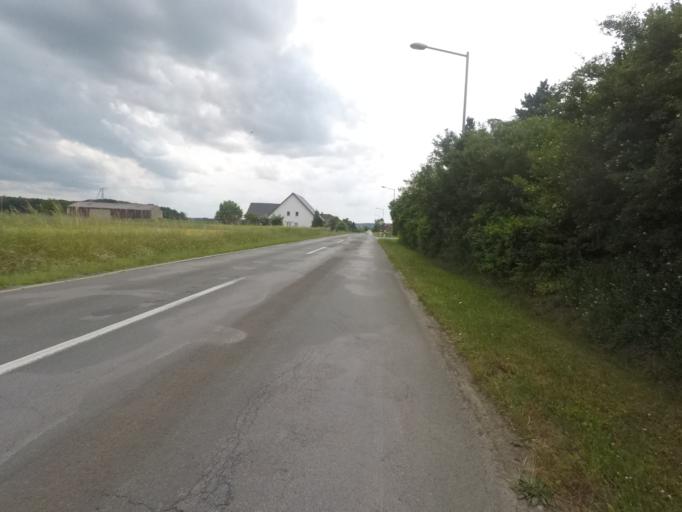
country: DE
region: North Rhine-Westphalia
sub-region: Regierungsbezirk Detmold
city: Rodinghausen
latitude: 52.2032
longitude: 8.4873
